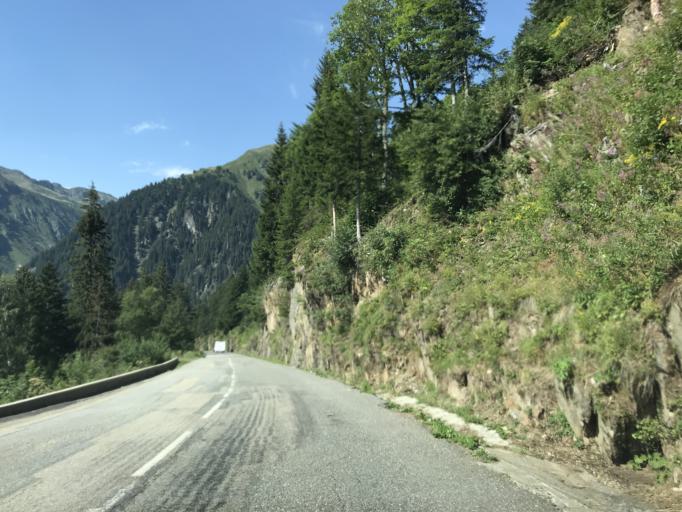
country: FR
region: Rhone-Alpes
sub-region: Departement de la Savoie
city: Beaufort
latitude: 45.6999
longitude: 6.6338
